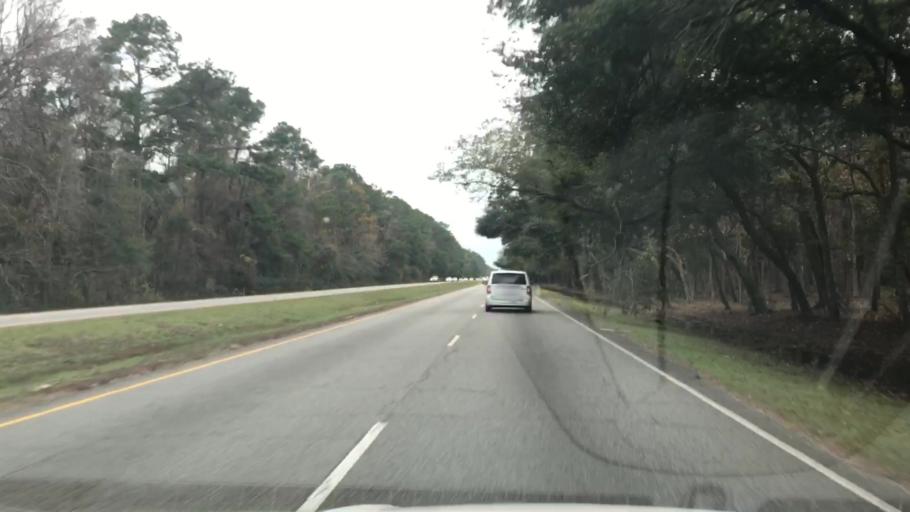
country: US
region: South Carolina
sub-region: Georgetown County
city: Murrells Inlet
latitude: 33.5177
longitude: -79.0706
